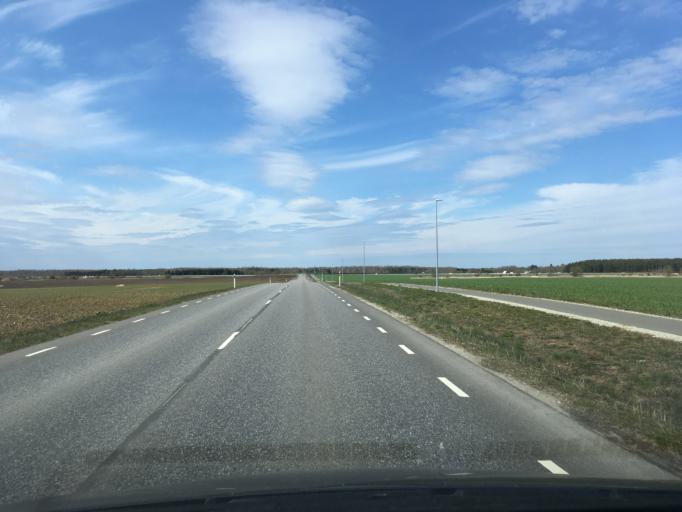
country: EE
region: Harju
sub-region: Maardu linn
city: Maardu
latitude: 59.4435
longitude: 25.0694
